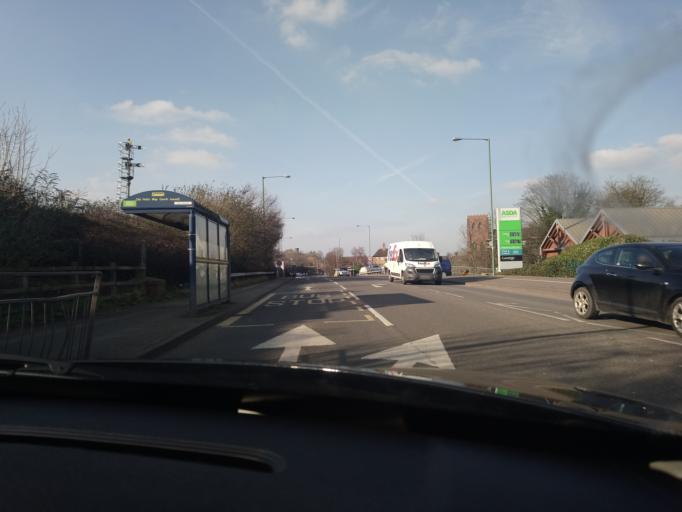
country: GB
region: England
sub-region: Shropshire
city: Shrewsbury
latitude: 52.7052
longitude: -2.7434
